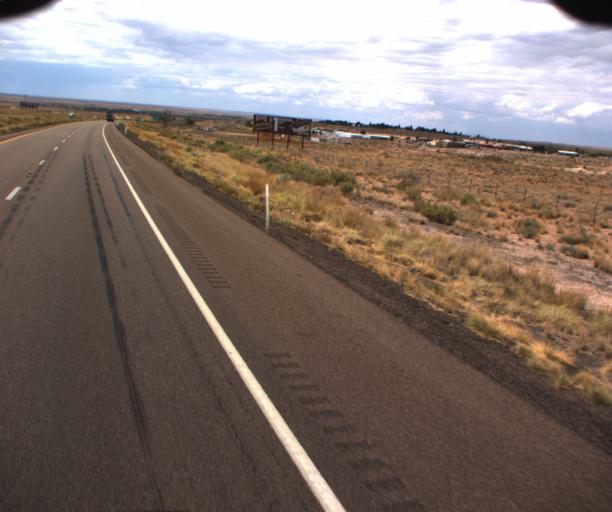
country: US
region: Arizona
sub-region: Navajo County
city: Holbrook
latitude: 34.9196
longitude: -110.1423
